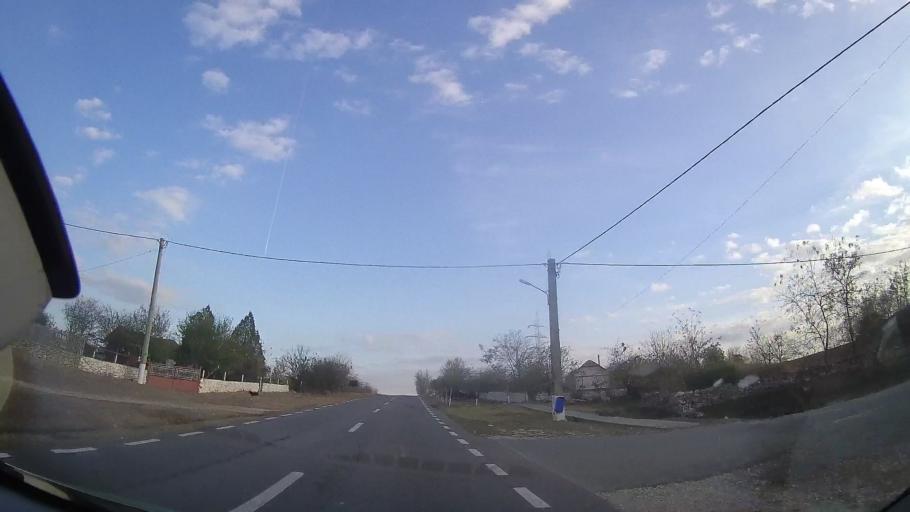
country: RO
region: Constanta
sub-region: Comuna Chirnogeni
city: Plopeni
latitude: 43.9590
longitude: 28.1457
